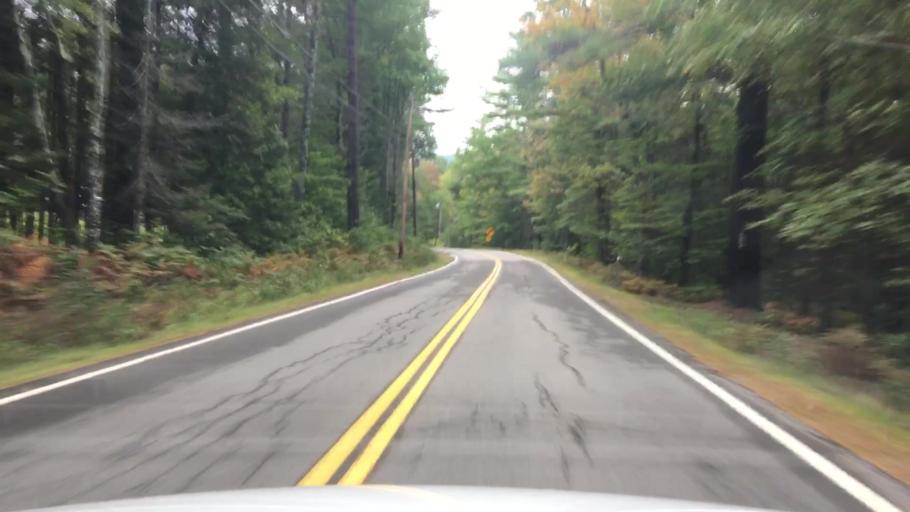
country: US
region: New Hampshire
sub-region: Carroll County
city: Effingham
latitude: 43.7320
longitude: -71.0045
